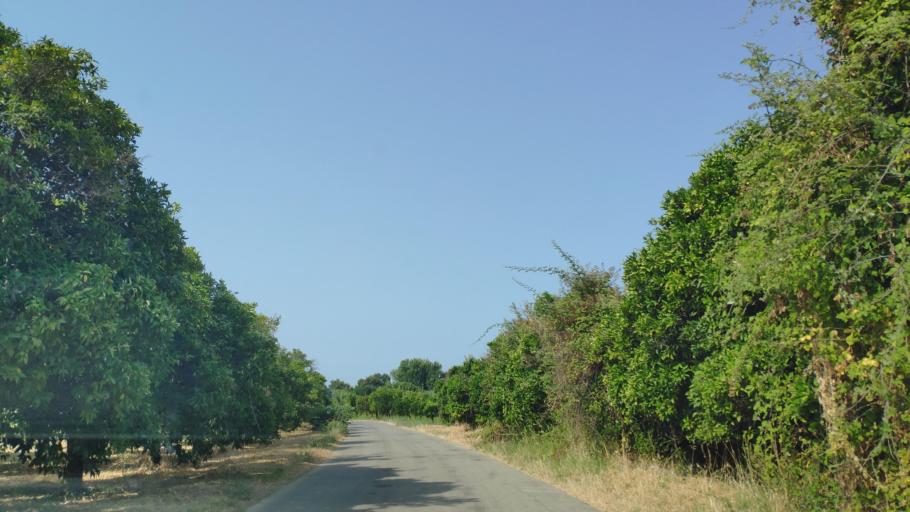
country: GR
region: Epirus
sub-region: Nomos Artas
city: Kompoti
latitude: 39.0788
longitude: 21.0854
